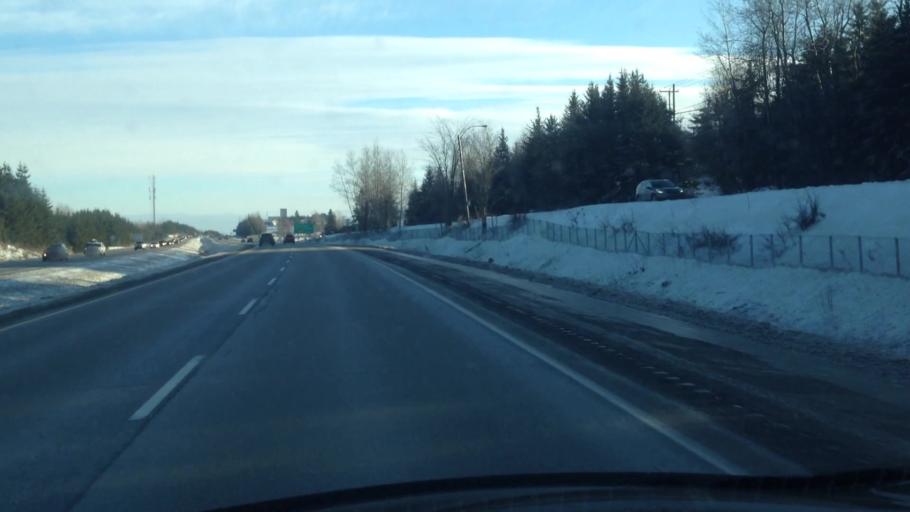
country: CA
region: Quebec
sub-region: Laurentides
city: Saint-Jerome
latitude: 45.8138
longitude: -74.0488
